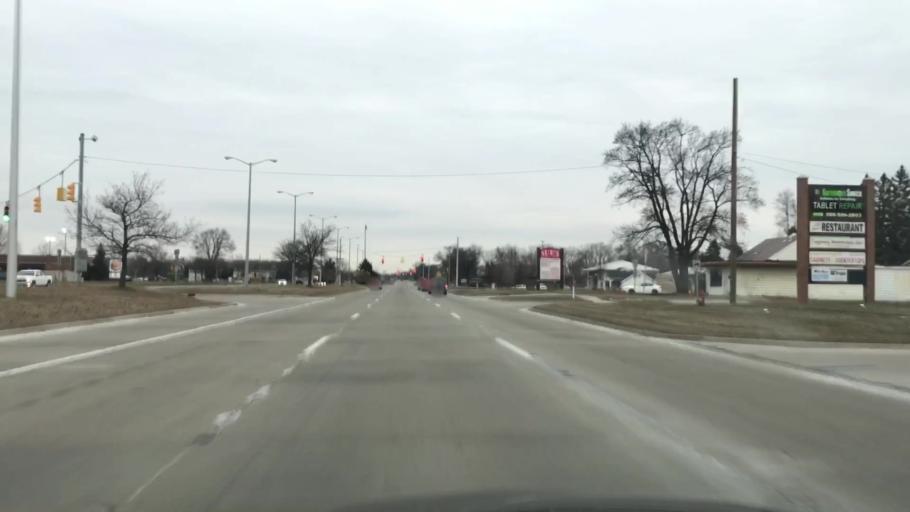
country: US
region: Michigan
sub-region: Macomb County
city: Utica
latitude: 42.6169
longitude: -83.0515
